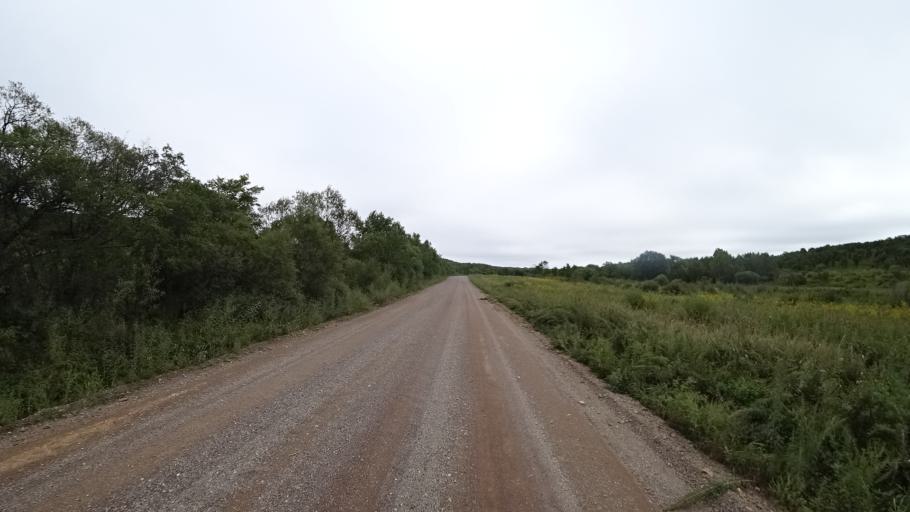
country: RU
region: Primorskiy
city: Ivanovka
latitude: 44.0502
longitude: 132.4876
